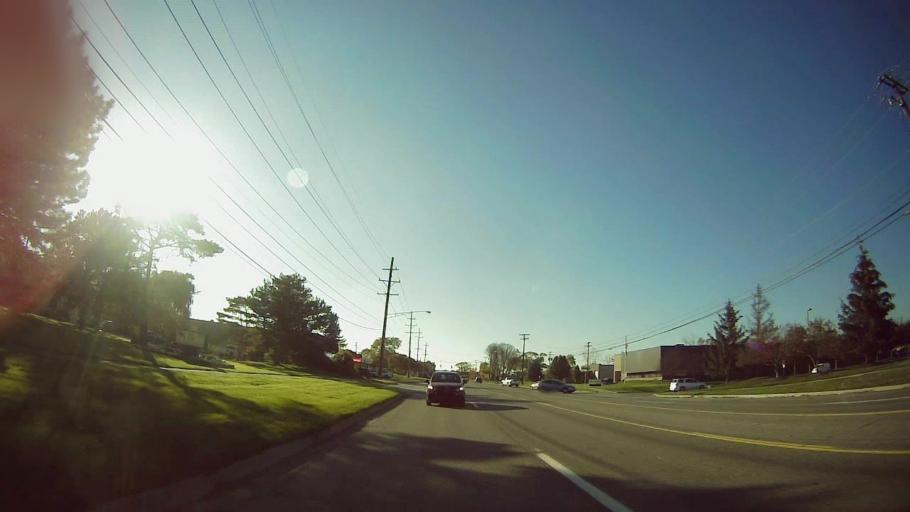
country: US
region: Michigan
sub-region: Oakland County
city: Clawson
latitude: 42.5490
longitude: -83.1118
